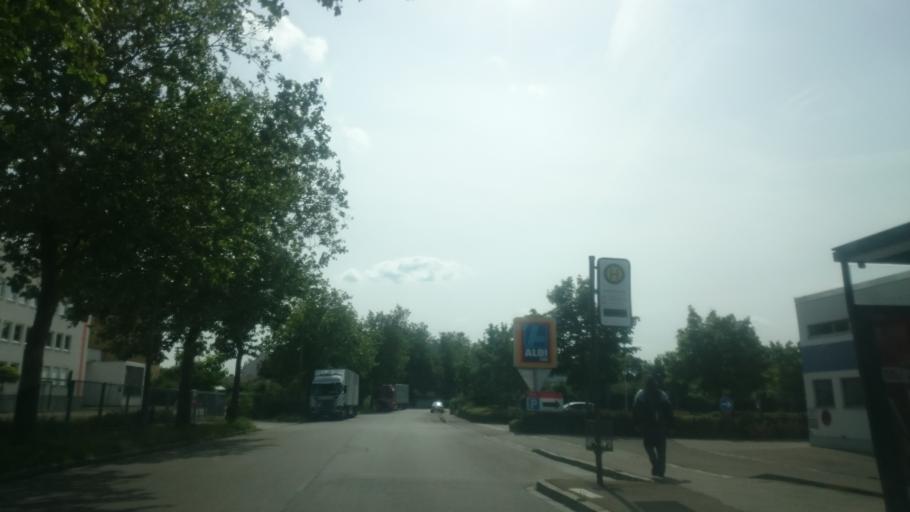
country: DE
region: Bavaria
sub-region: Swabia
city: Augsburg
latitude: 48.3941
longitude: 10.9267
